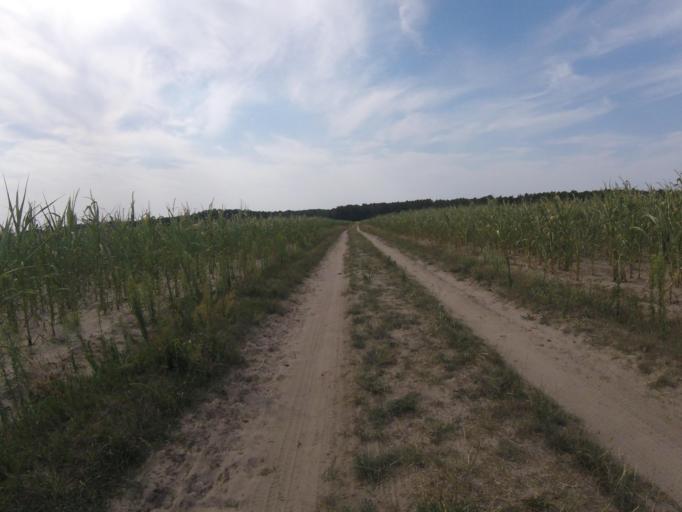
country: DE
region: Brandenburg
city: Wildau
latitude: 52.3087
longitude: 13.7285
